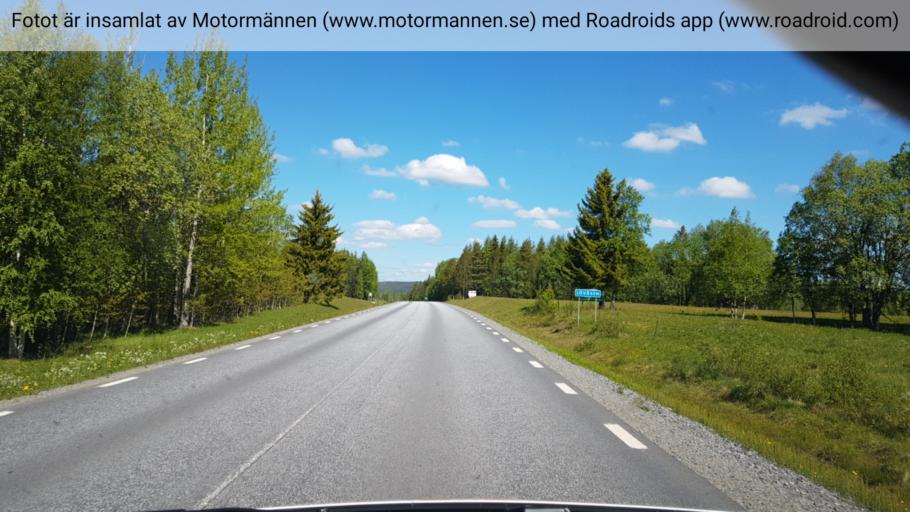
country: SE
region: Vaesterbotten
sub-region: Vilhelmina Kommun
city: Vilhelmina
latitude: 64.5717
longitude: 16.7447
